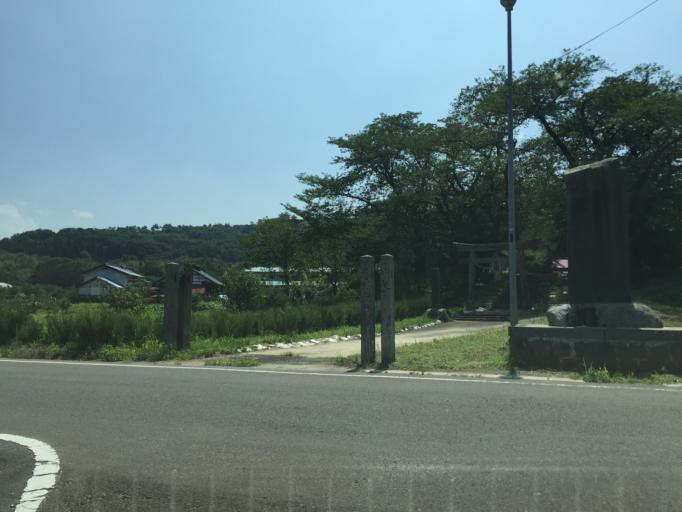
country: JP
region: Fukushima
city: Fukushima-shi
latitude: 37.7019
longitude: 140.4469
